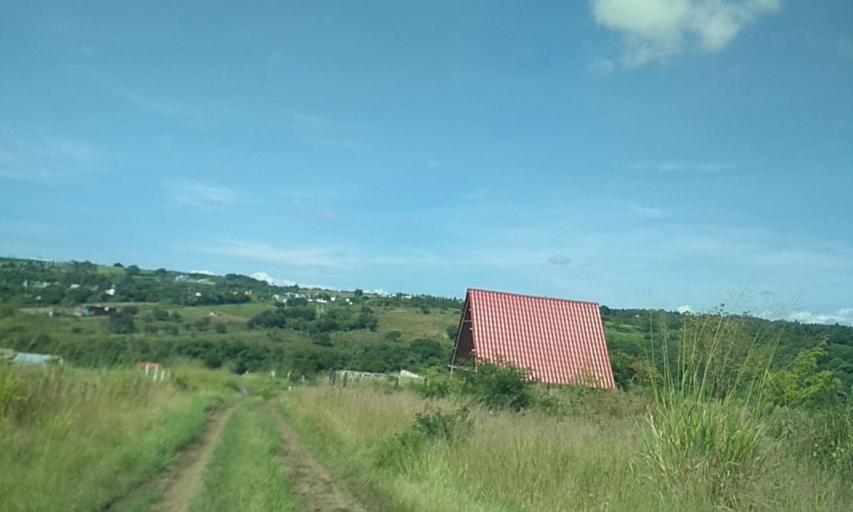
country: MX
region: Veracruz
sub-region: Emiliano Zapata
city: Dos Rios
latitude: 19.5069
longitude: -96.8179
